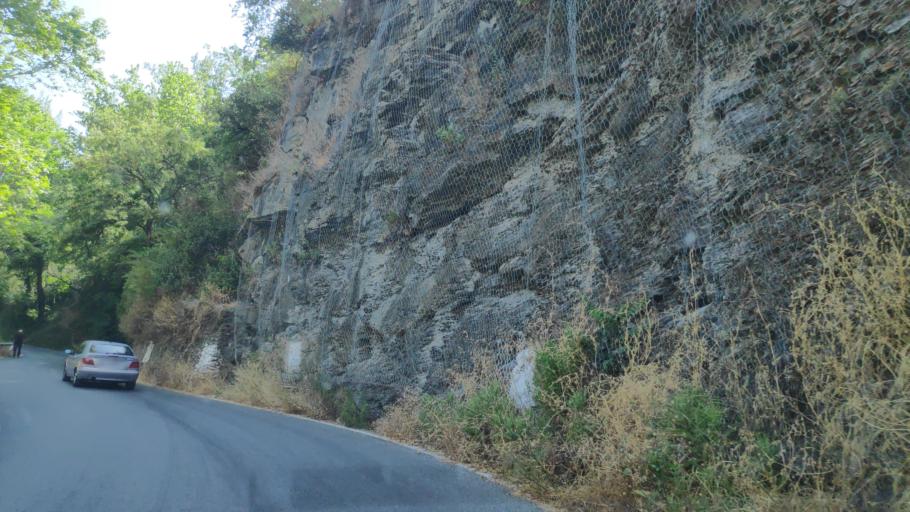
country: ES
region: Andalusia
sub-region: Provincia de Granada
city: Pampaneira
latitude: 36.9425
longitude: -3.3642
